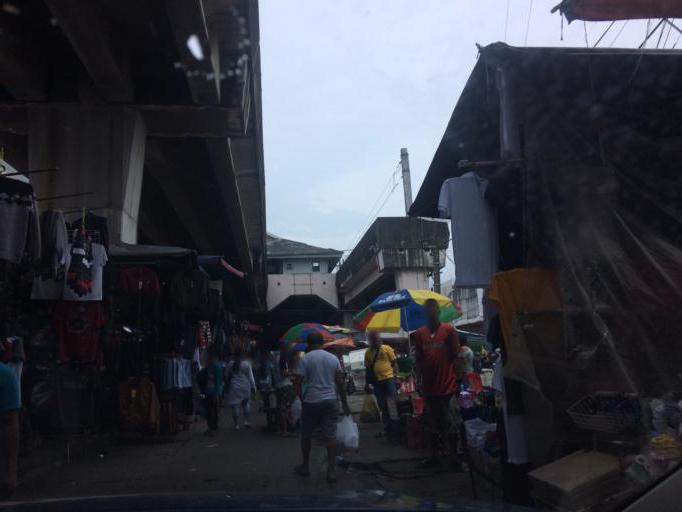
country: PH
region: Metro Manila
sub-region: Makati City
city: Makati City
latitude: 14.5334
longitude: 120.9978
